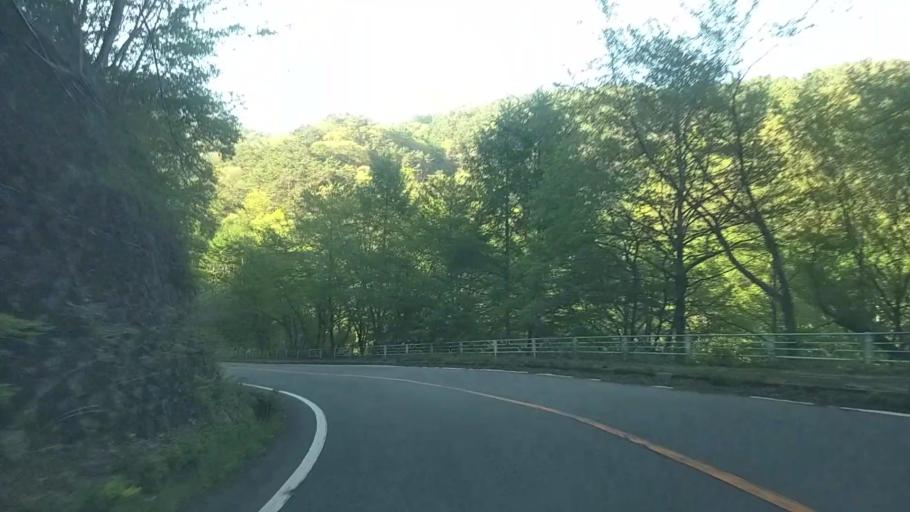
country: JP
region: Yamanashi
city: Nirasaki
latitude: 35.9061
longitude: 138.3782
